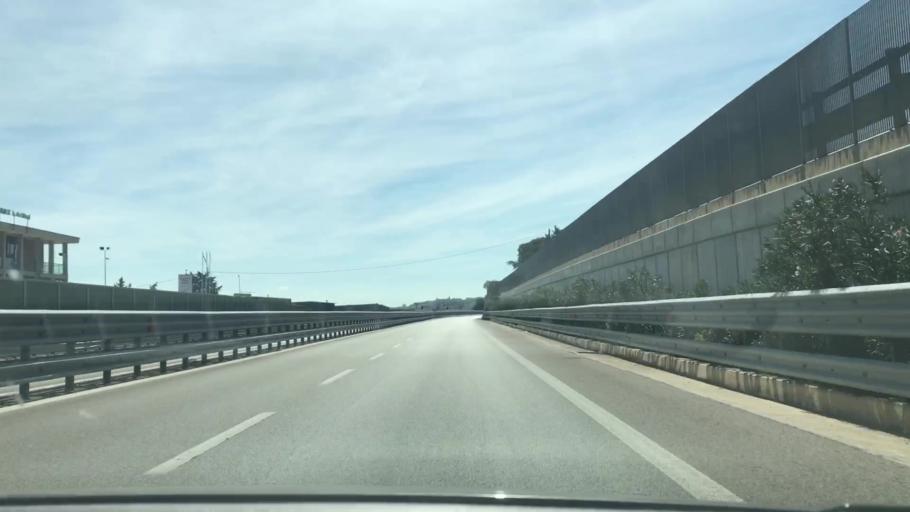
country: IT
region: Basilicate
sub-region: Provincia di Matera
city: Matera
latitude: 40.6971
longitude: 16.5900
